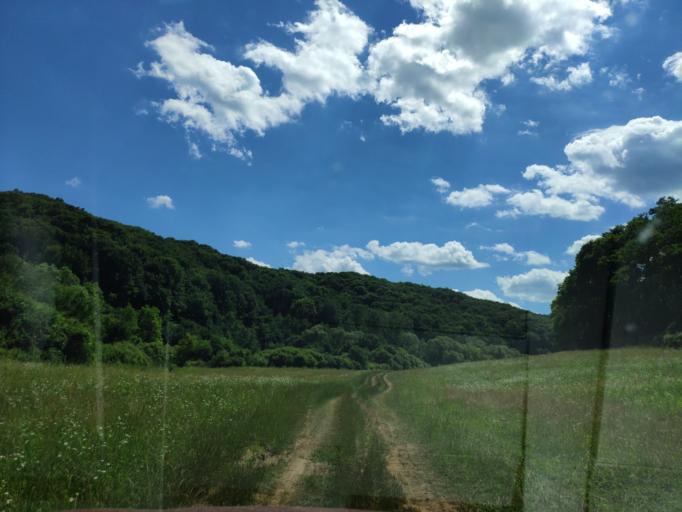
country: HU
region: Borsod-Abauj-Zemplen
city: Arlo
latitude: 48.2604
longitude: 20.1879
